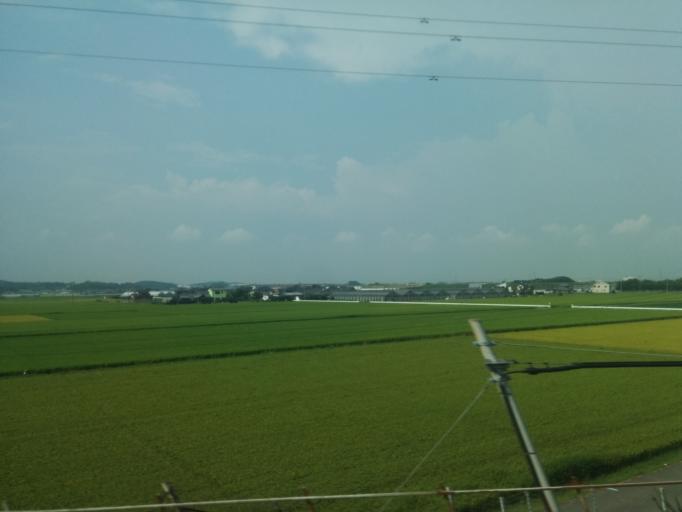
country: JP
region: Aichi
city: Anjo
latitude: 34.9070
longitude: 137.1176
